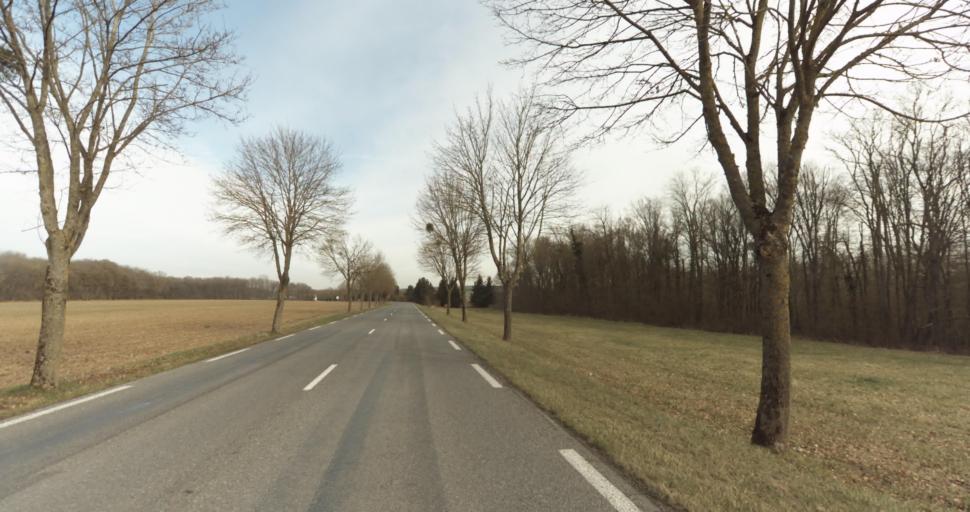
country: FR
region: Lorraine
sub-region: Departement de Meurthe-et-Moselle
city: Jarny
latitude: 49.1313
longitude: 5.8924
